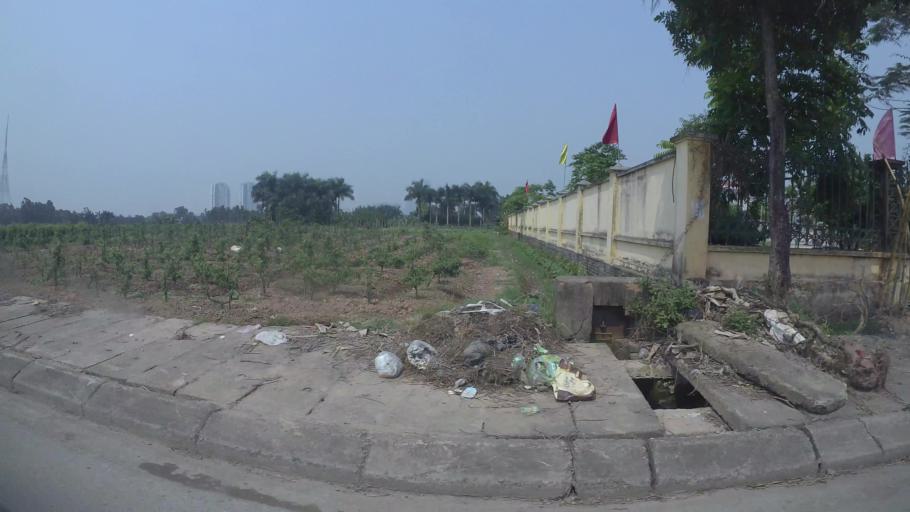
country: VN
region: Ha Noi
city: Ha Dong
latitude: 20.9924
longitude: 105.7682
